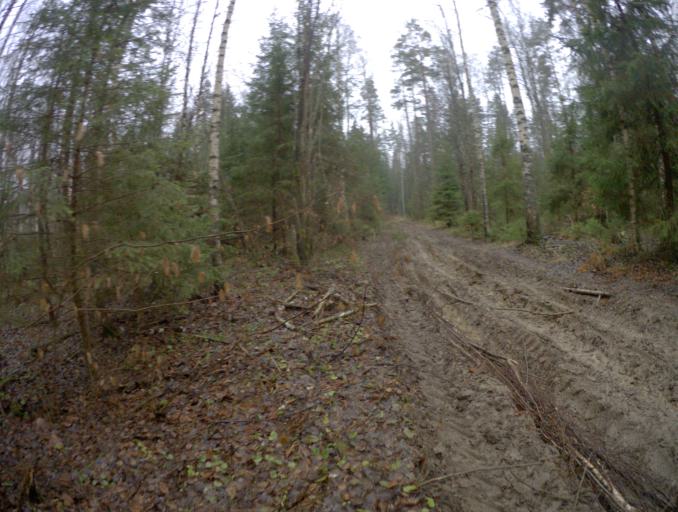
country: RU
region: Vladimir
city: Golovino
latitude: 55.9992
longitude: 40.4715
